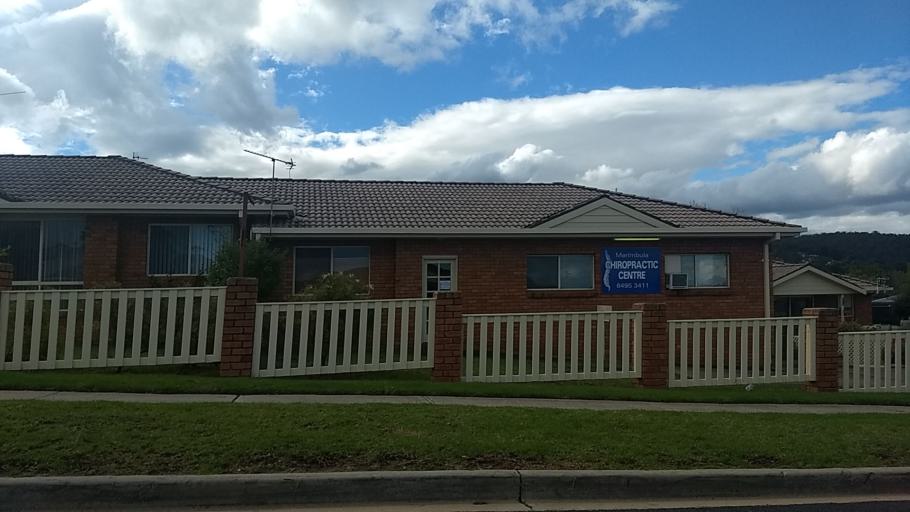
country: AU
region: New South Wales
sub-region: Bega Valley
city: Merimbula
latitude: -36.8885
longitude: 149.9055
